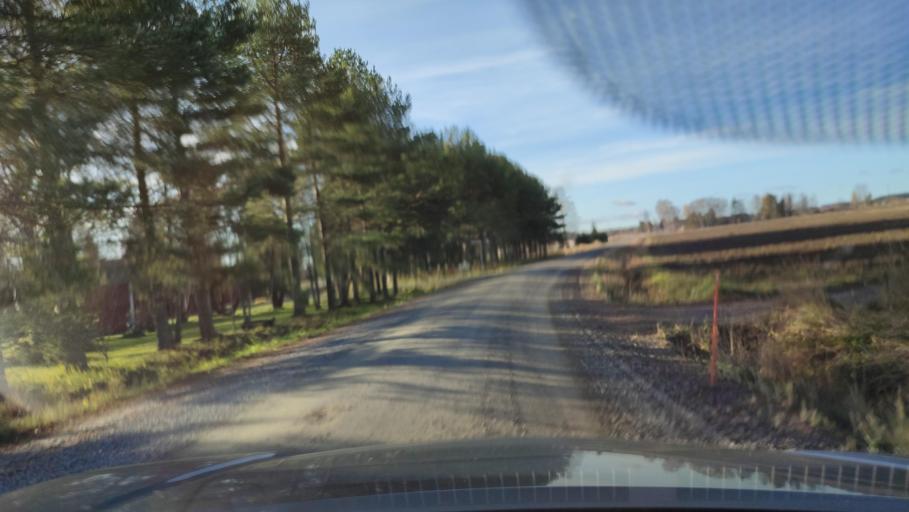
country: FI
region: Southern Ostrobothnia
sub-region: Suupohja
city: Teuva
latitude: 62.4622
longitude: 21.6954
